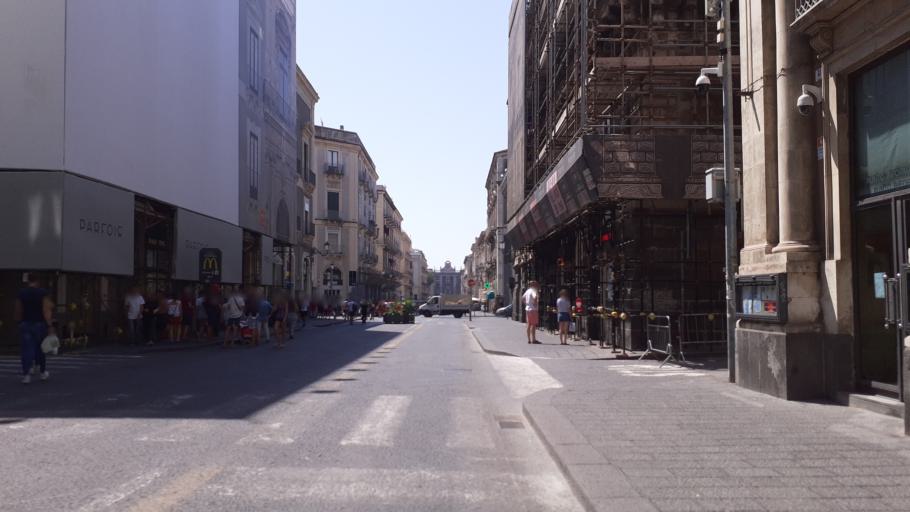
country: IT
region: Sicily
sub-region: Catania
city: Catania
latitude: 37.5056
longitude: 15.0867
